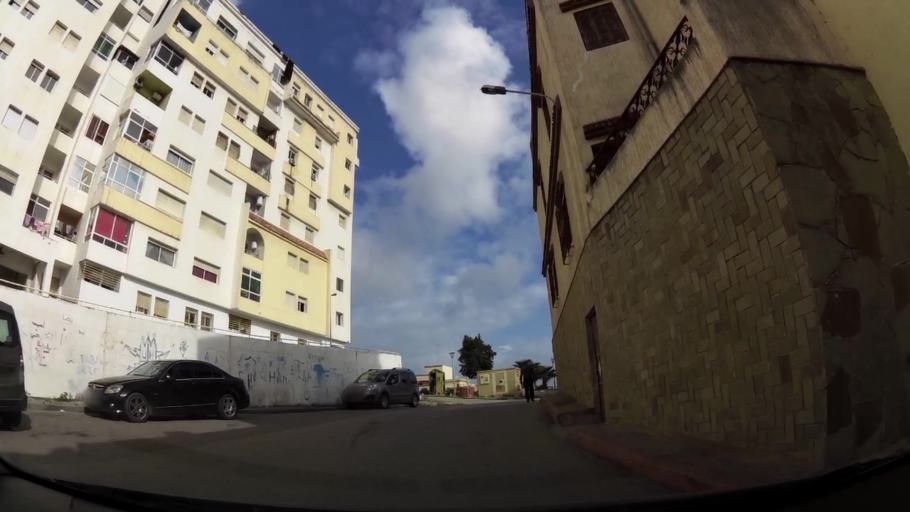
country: MA
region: Tanger-Tetouan
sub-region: Tanger-Assilah
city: Tangier
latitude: 35.7659
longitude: -5.8310
